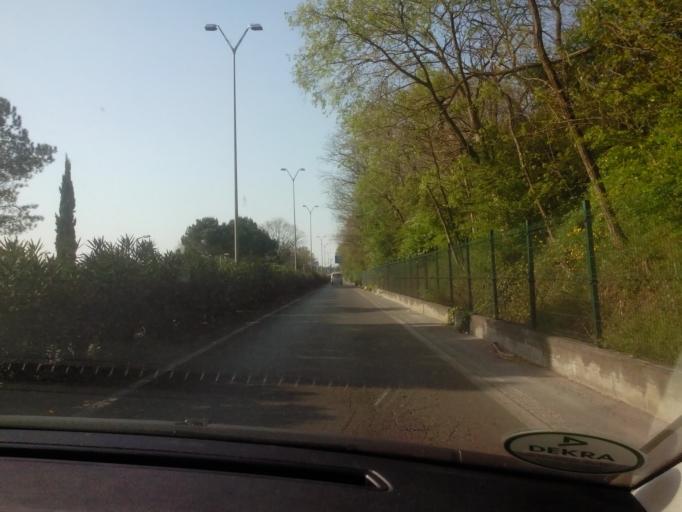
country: IT
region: Lombardy
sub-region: Provincia di Brescia
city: Desenzano del Garda
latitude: 45.4631
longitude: 10.5256
